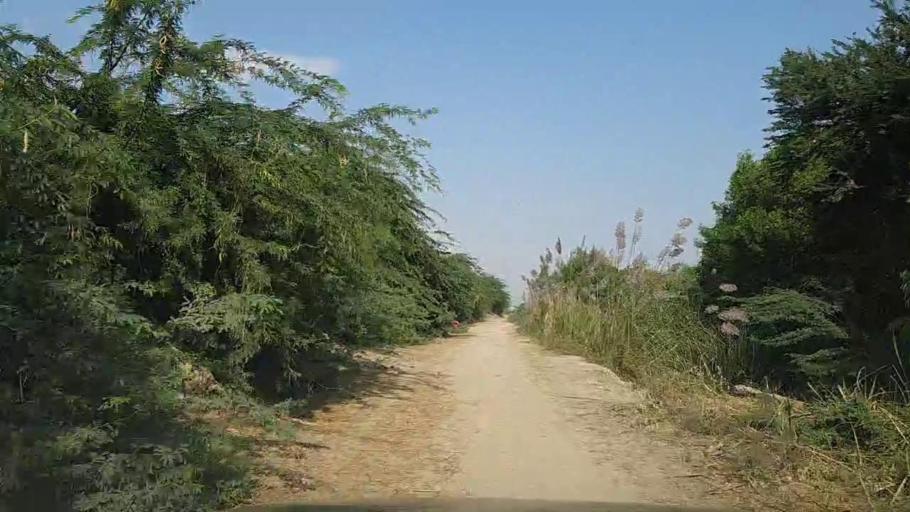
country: PK
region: Sindh
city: Thatta
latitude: 24.7890
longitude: 67.8184
